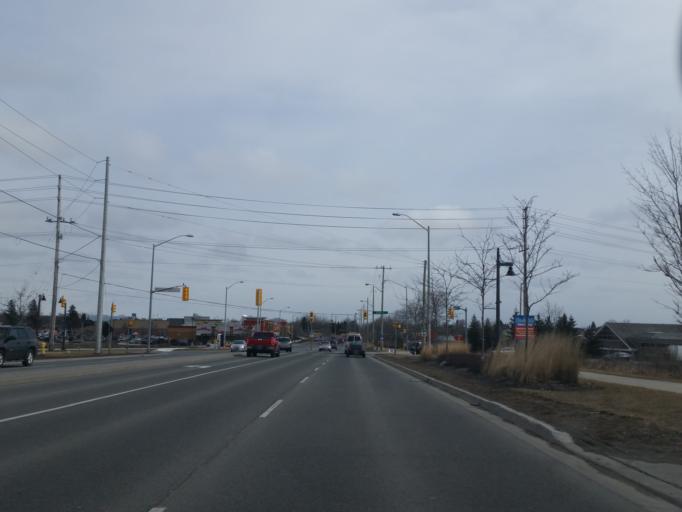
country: CA
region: Ontario
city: Oshawa
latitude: 43.9093
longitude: -78.7133
